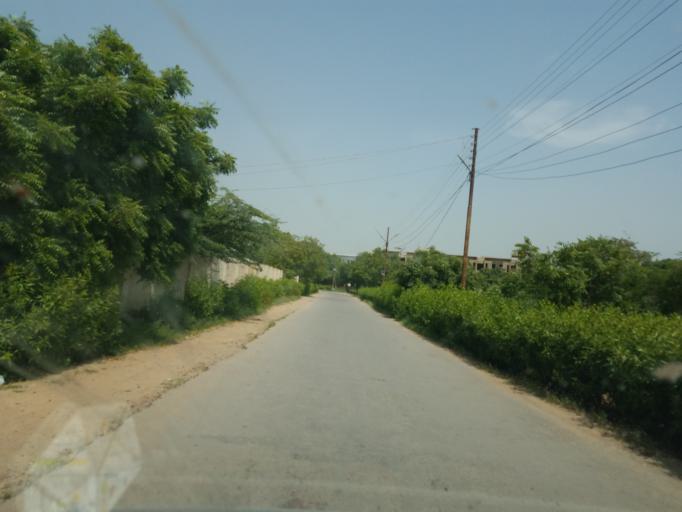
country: PK
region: Sindh
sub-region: Karachi District
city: Karachi
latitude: 24.9360
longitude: 67.1084
